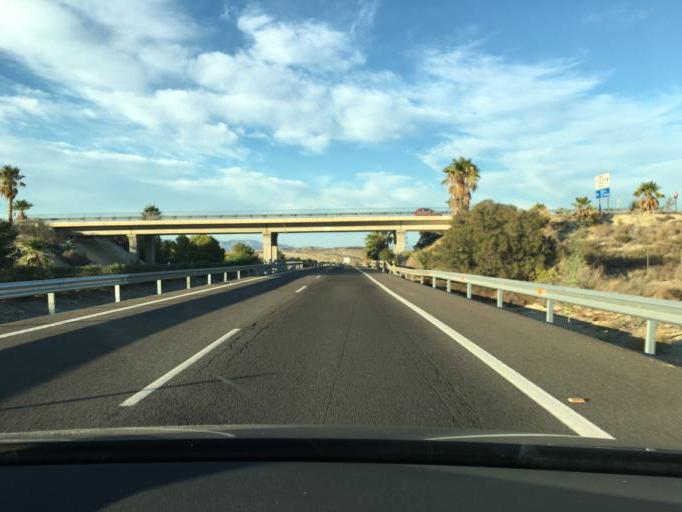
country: ES
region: Andalusia
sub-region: Provincia de Almeria
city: Turre
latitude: 37.1908
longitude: -1.9170
